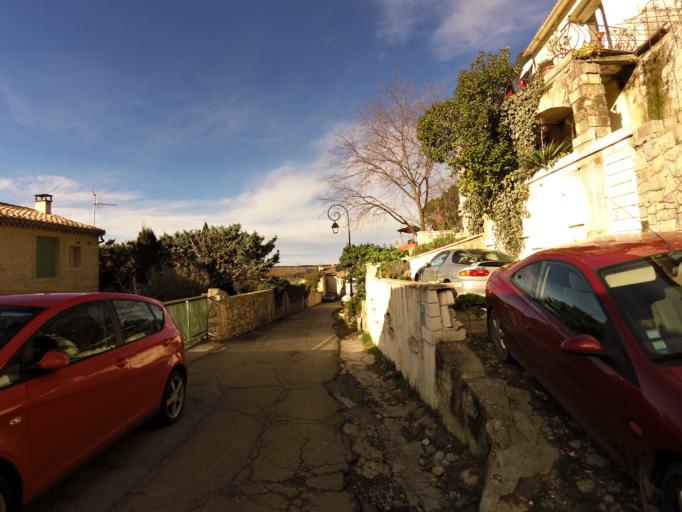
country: FR
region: Languedoc-Roussillon
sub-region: Departement du Gard
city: Langlade
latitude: 43.8015
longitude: 4.2484
